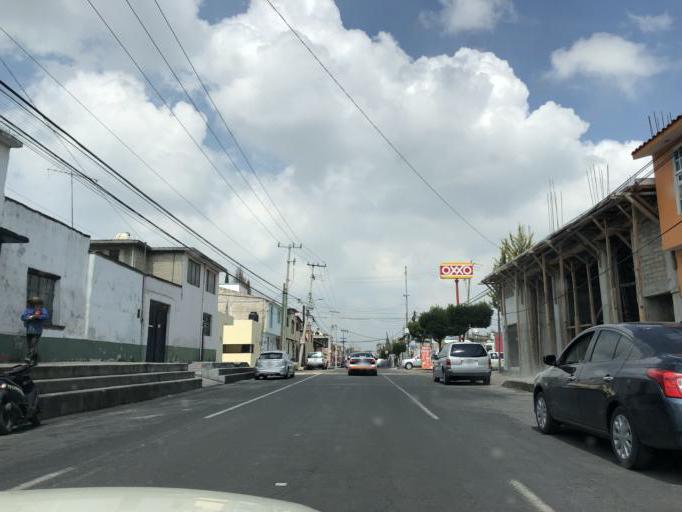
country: MX
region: Mexico
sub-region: Lerma
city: Nueva Ameyalco
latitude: 19.2858
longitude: -99.5059
